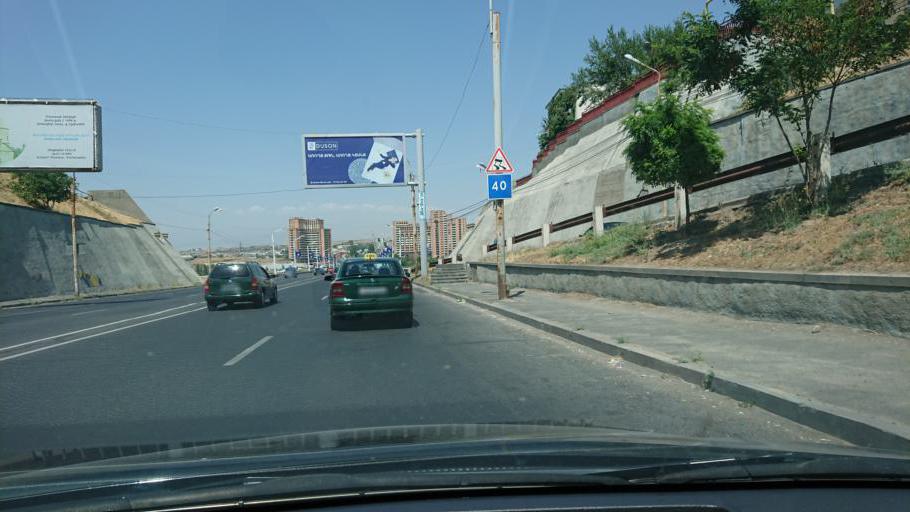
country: AM
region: Yerevan
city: Yerevan
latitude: 40.2072
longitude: 44.4956
